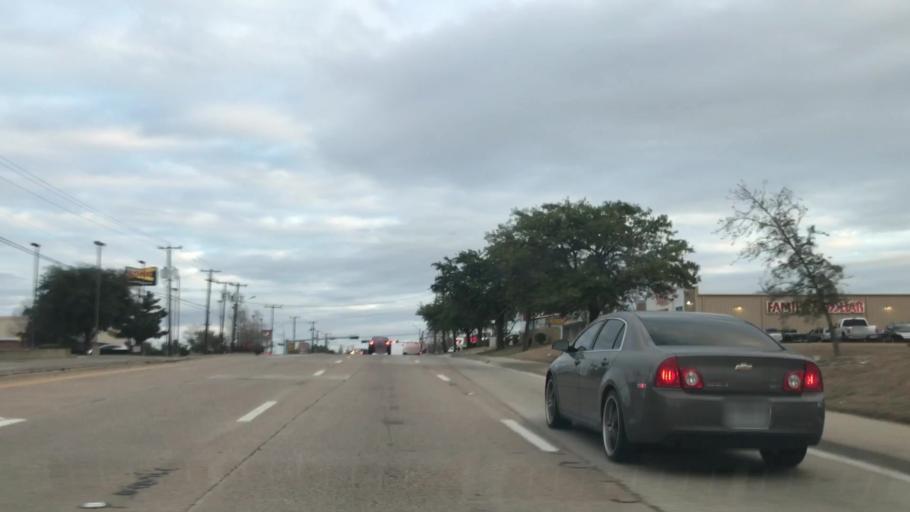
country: US
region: Texas
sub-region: Dallas County
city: Cockrell Hill
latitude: 32.6912
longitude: -96.8592
